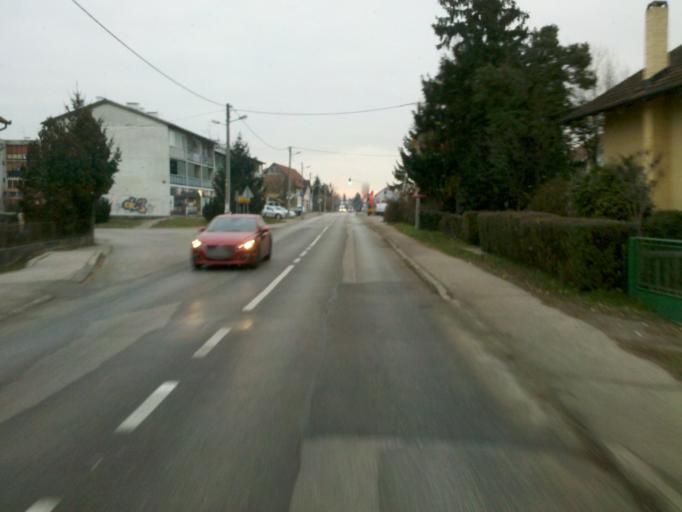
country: HR
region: Grad Zagreb
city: Lucko
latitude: 45.7611
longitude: 15.8833
